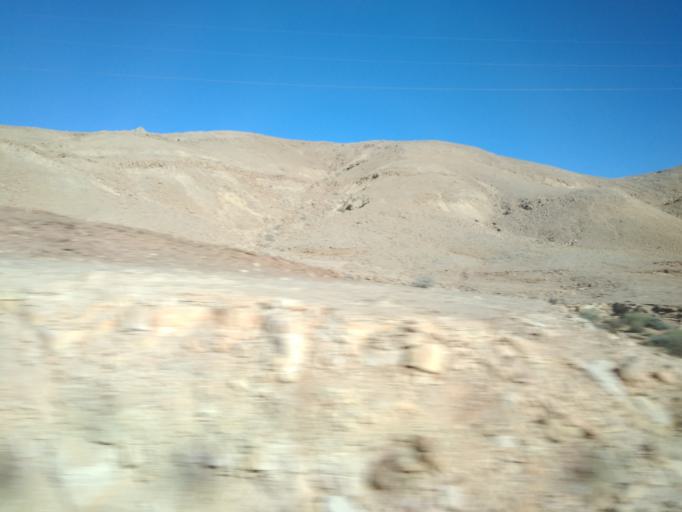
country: IL
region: Southern District
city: Eilat
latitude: 29.6231
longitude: 34.8787
